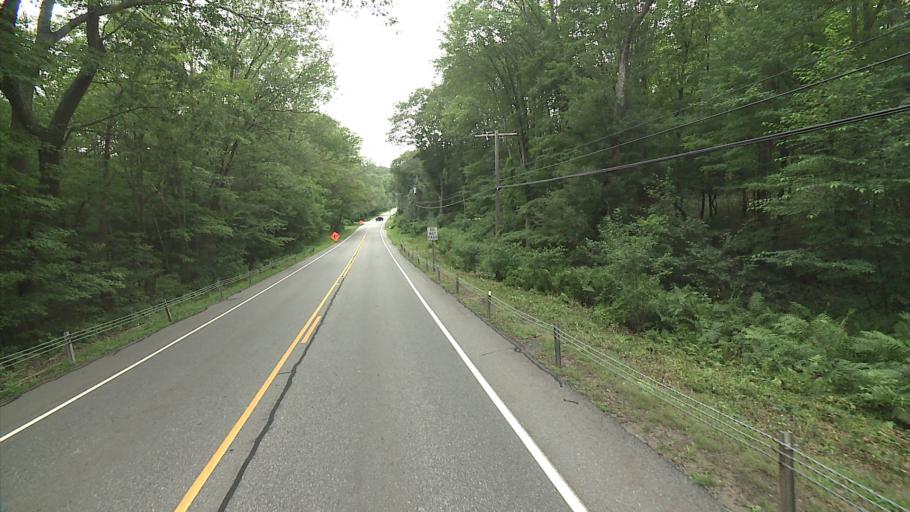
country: US
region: Connecticut
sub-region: Tolland County
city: Storrs
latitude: 41.8725
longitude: -72.2187
